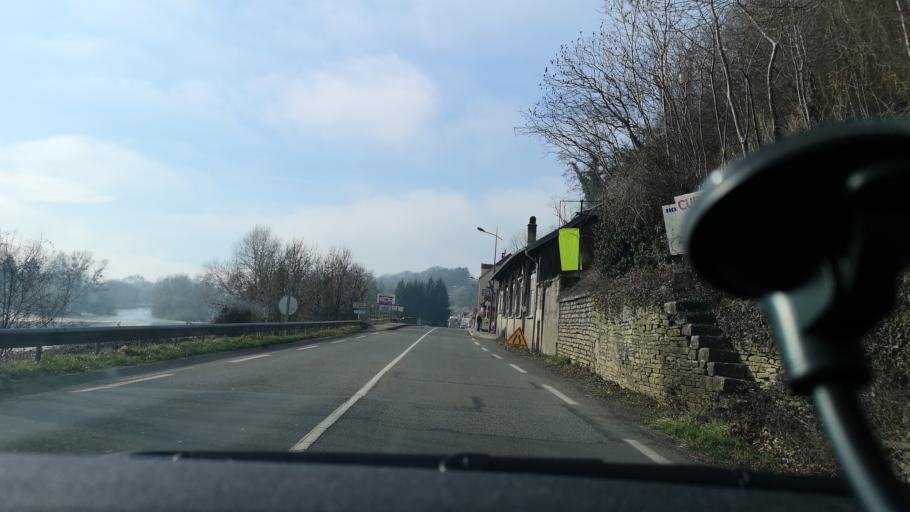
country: FR
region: Franche-Comte
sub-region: Departement du Doubs
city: Montenois
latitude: 47.4560
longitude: 6.5847
